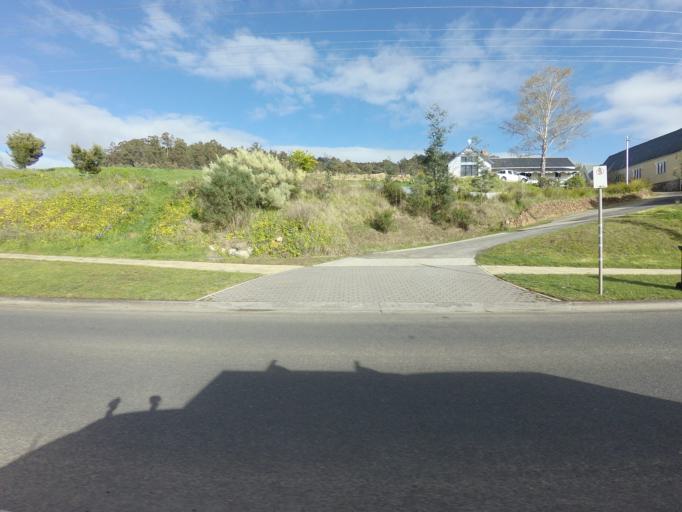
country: AU
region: Tasmania
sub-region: Huon Valley
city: Franklin
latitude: -43.0952
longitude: 147.0073
